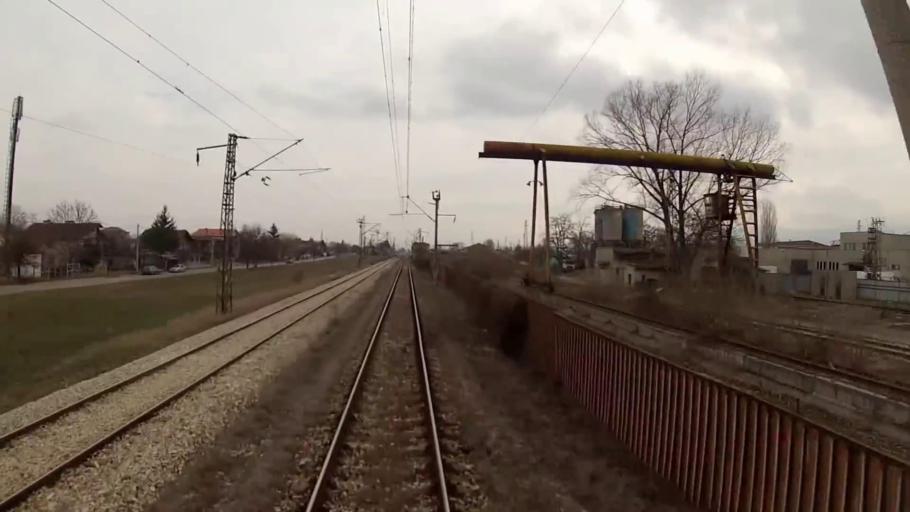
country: BG
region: Sofiya
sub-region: Obshtina Elin Pelin
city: Elin Pelin
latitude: 42.6613
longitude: 23.5008
